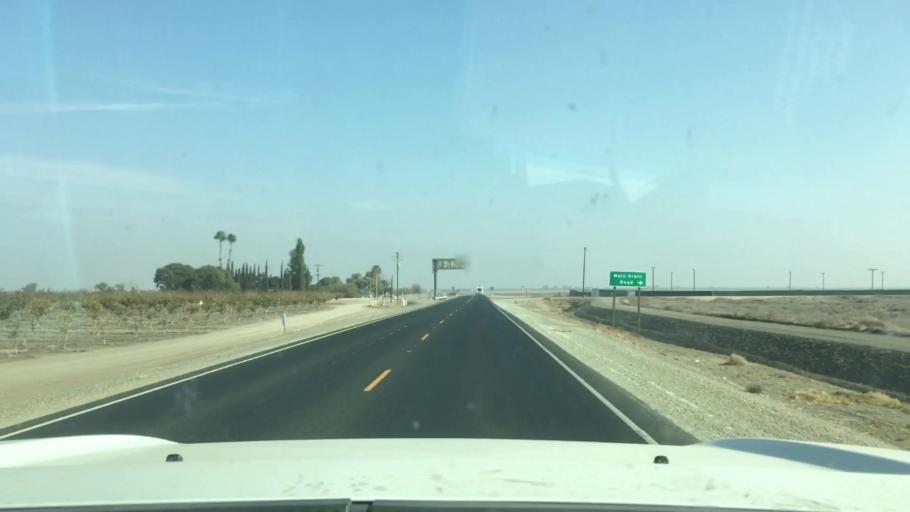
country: US
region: California
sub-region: Kern County
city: Lost Hills
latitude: 35.6160
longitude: -119.6196
